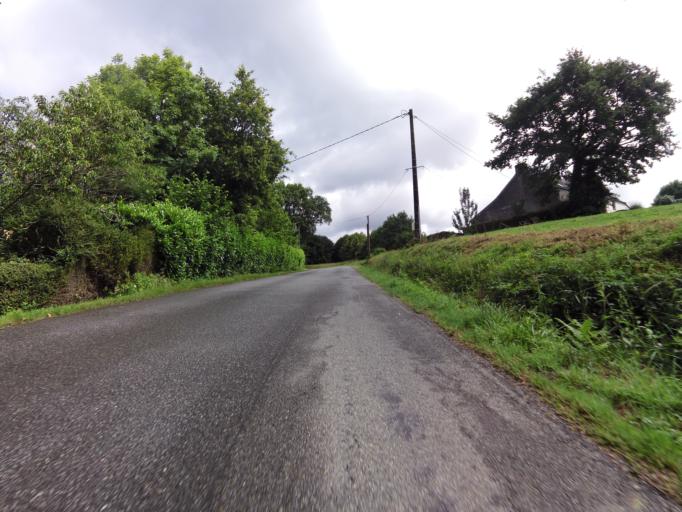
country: FR
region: Brittany
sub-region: Departement du Morbihan
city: Malansac
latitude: 47.7077
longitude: -2.2800
